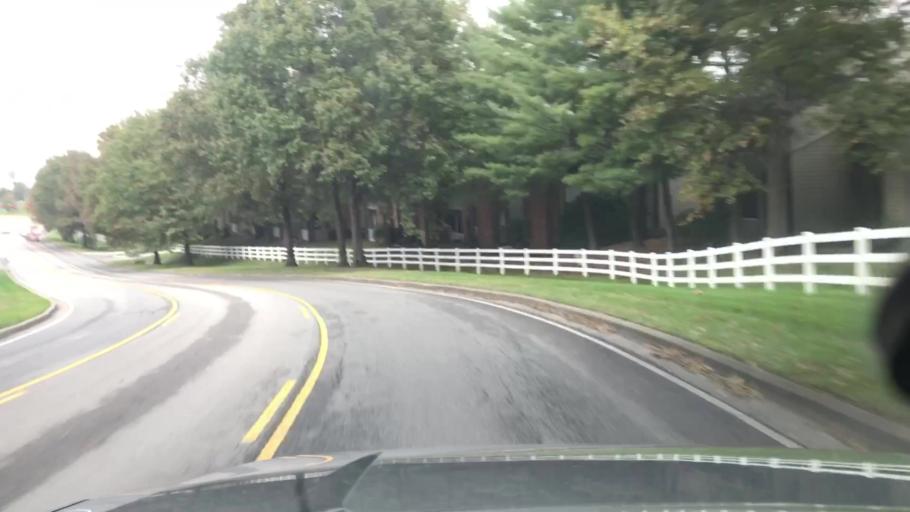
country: US
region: Tennessee
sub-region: Williamson County
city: Franklin
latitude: 35.9237
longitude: -86.8251
